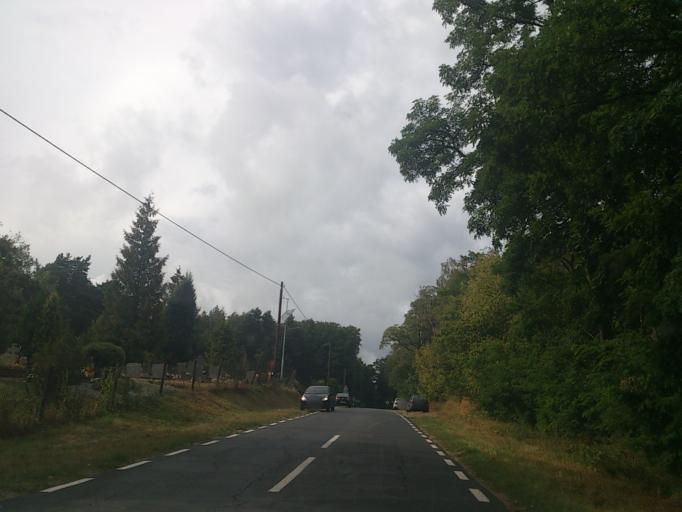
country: PL
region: Greater Poland Voivodeship
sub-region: Powiat poznanski
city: Pobiedziska
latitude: 52.5071
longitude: 17.2074
